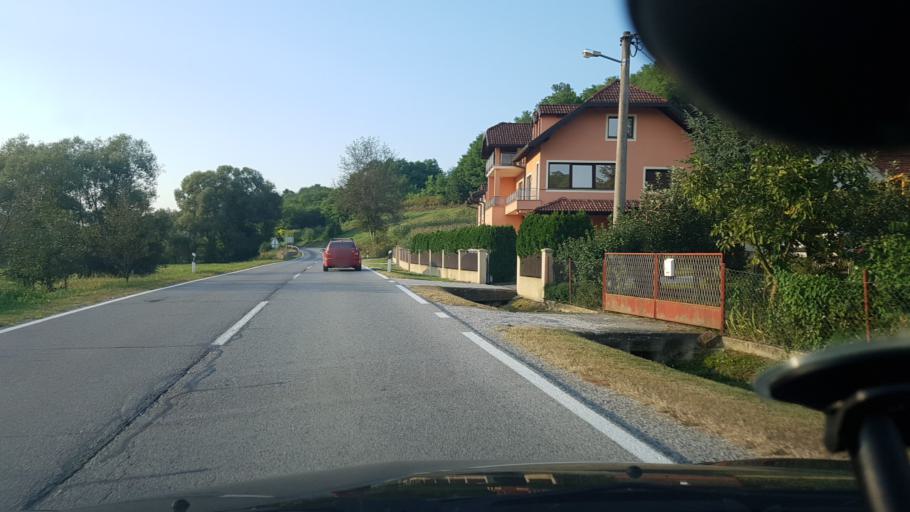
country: HR
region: Krapinsko-Zagorska
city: Pregrada
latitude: 46.1226
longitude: 15.8051
